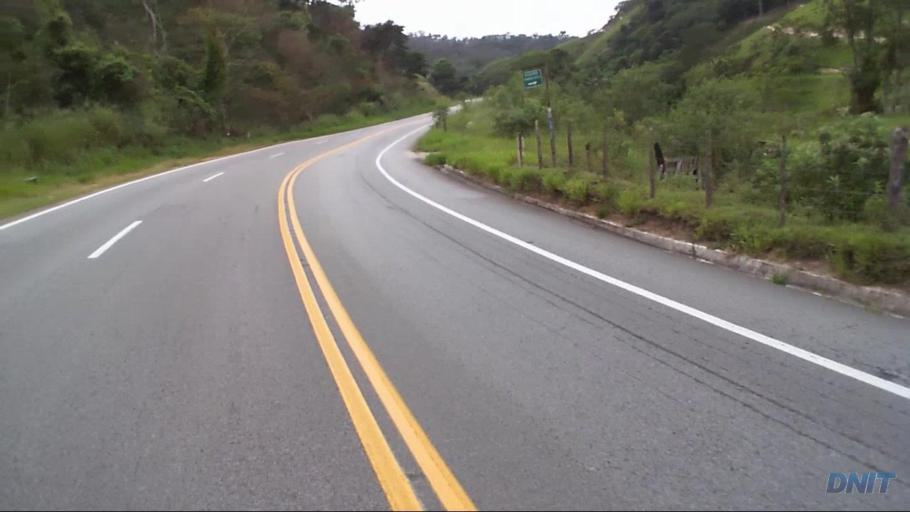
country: BR
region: Minas Gerais
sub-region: Nova Era
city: Nova Era
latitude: -19.6281
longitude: -42.8731
